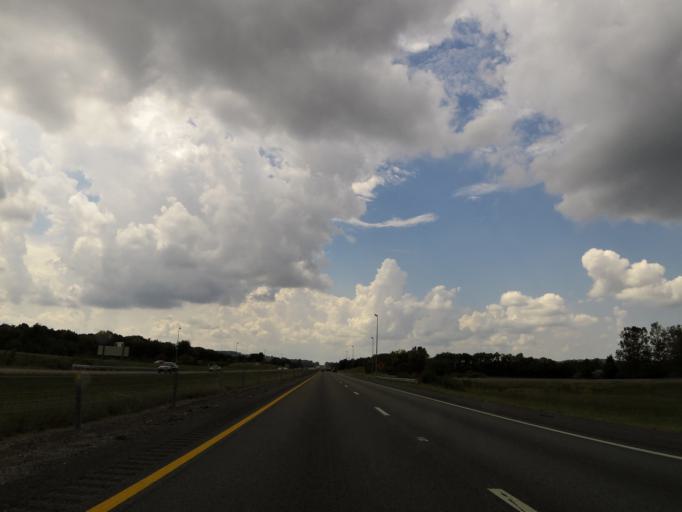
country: US
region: Tennessee
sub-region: Wilson County
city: Lebanon
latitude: 36.1831
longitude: -86.3280
